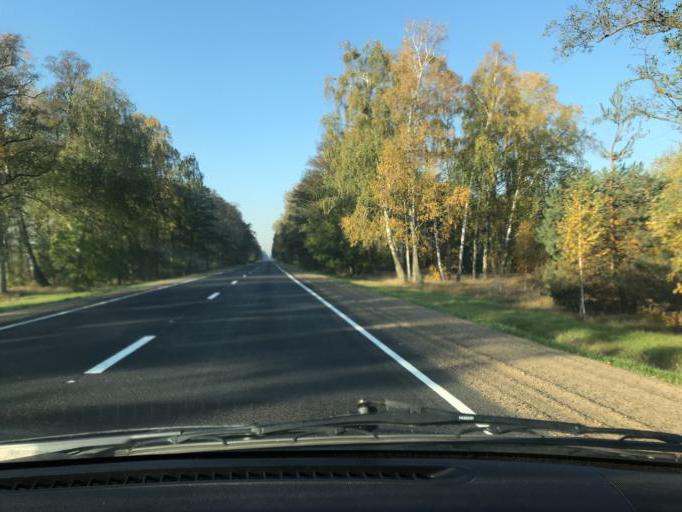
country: BY
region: Brest
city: Baranovichi
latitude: 52.8787
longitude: 25.7590
